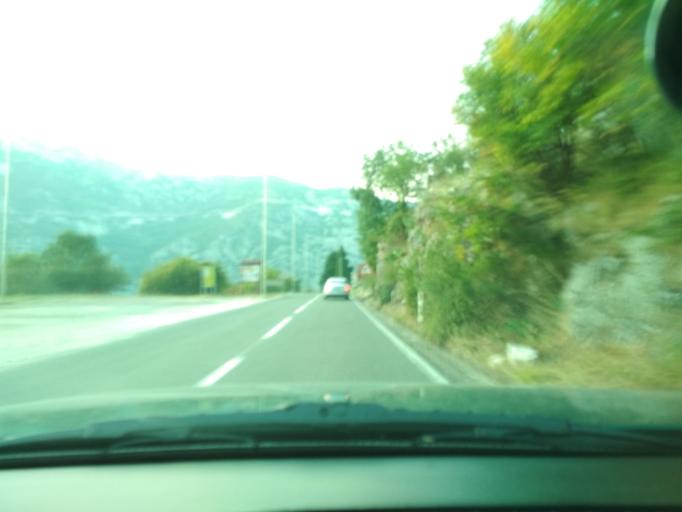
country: ME
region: Kotor
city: Risan
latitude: 42.5043
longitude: 18.6943
